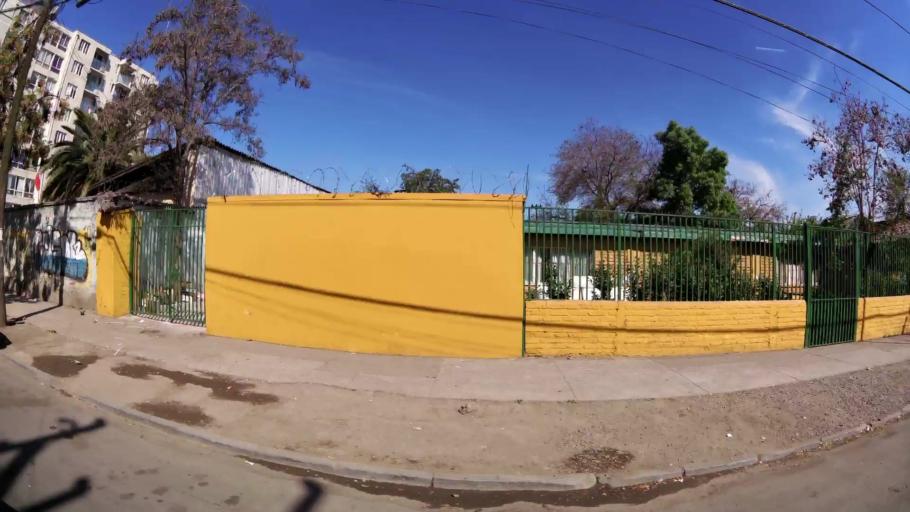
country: CL
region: Santiago Metropolitan
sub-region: Provincia de Santiago
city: Santiago
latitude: -33.4232
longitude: -70.6613
